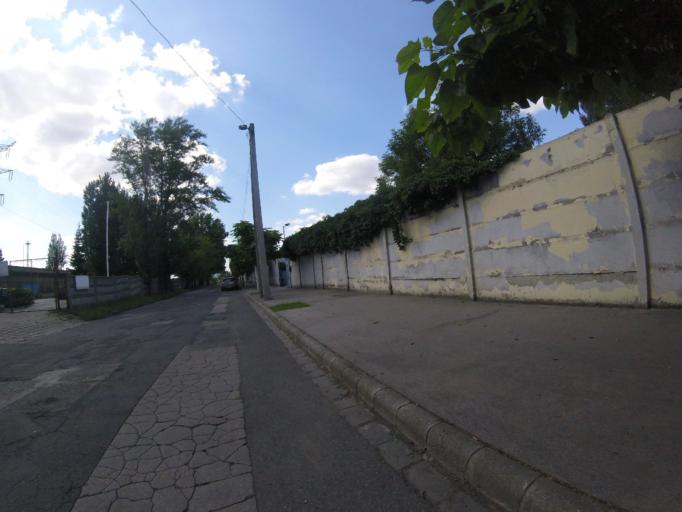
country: HU
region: Budapest
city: Budapest IV. keruelet
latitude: 47.5487
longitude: 19.0940
